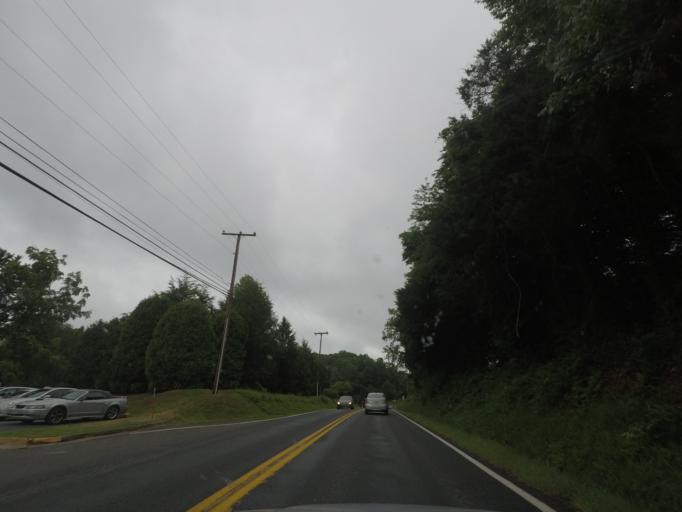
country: US
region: Virginia
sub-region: Fluvanna County
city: Palmyra
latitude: 37.8630
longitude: -78.2635
